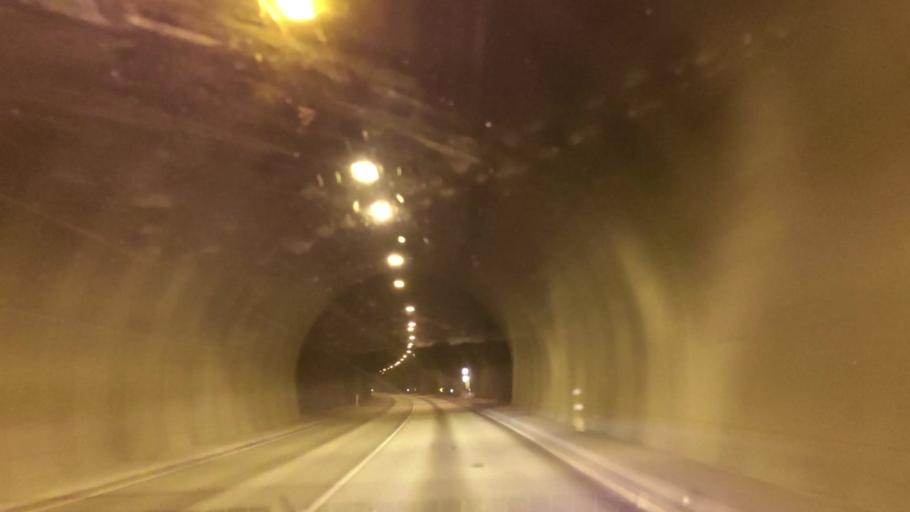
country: IS
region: Capital Region
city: Reykjavik
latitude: 64.2894
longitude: -21.8536
